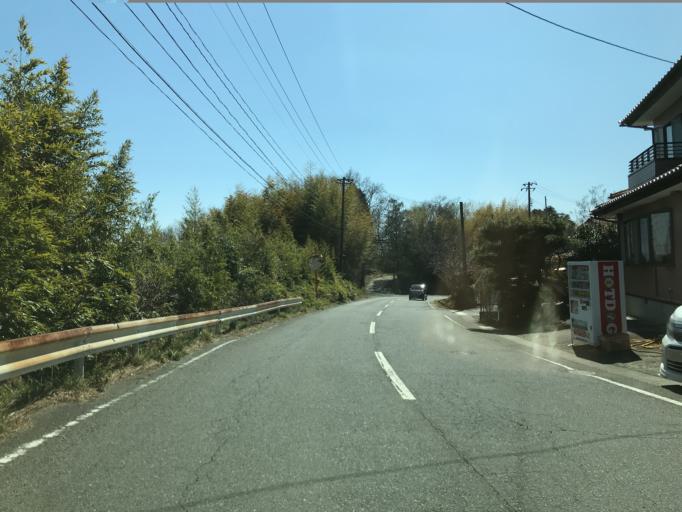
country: JP
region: Fukushima
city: Iwaki
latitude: 37.0494
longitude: 140.8475
